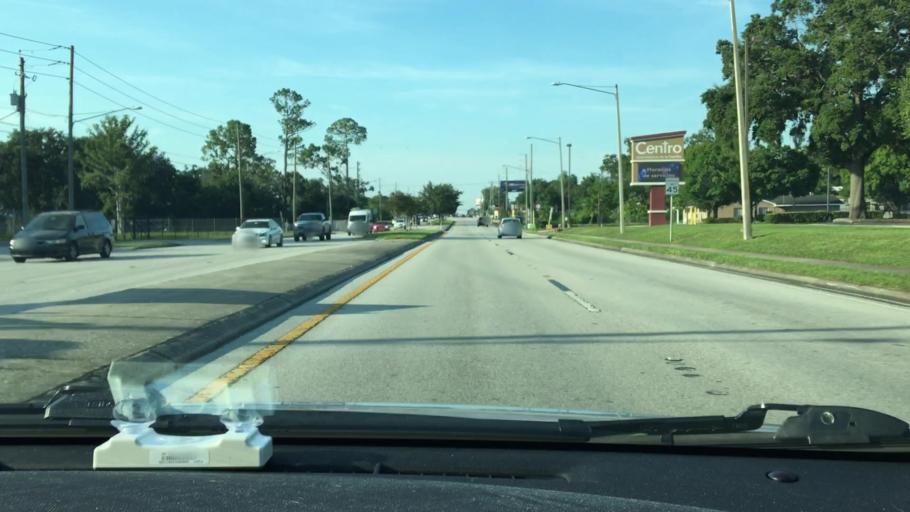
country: US
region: Florida
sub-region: Orange County
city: Union Park
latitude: 28.5752
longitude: -81.2862
